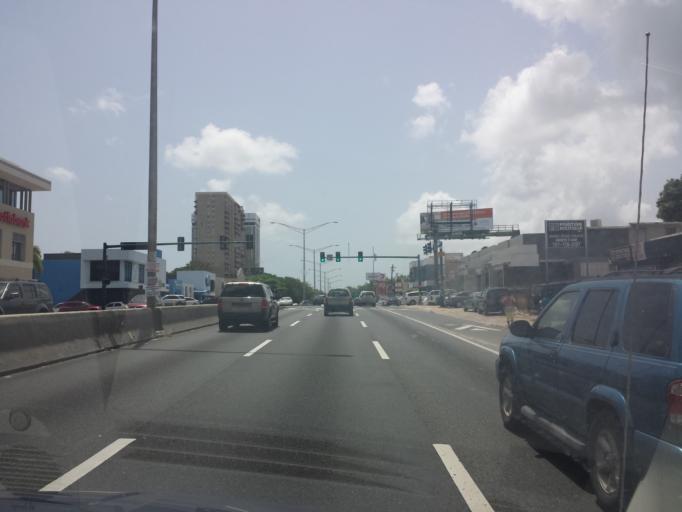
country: PR
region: Catano
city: Catano
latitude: 18.4075
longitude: -66.0618
